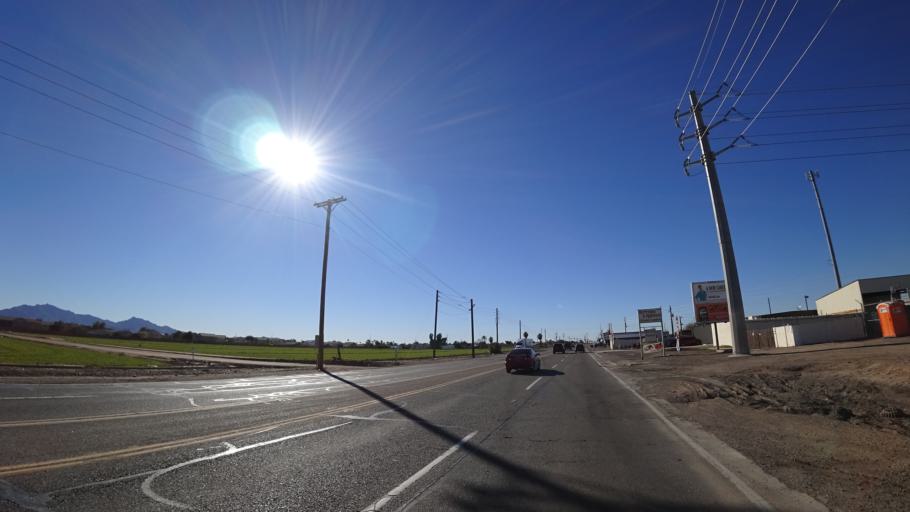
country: US
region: Arizona
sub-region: Maricopa County
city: Tolleson
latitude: 33.4356
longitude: -112.2850
